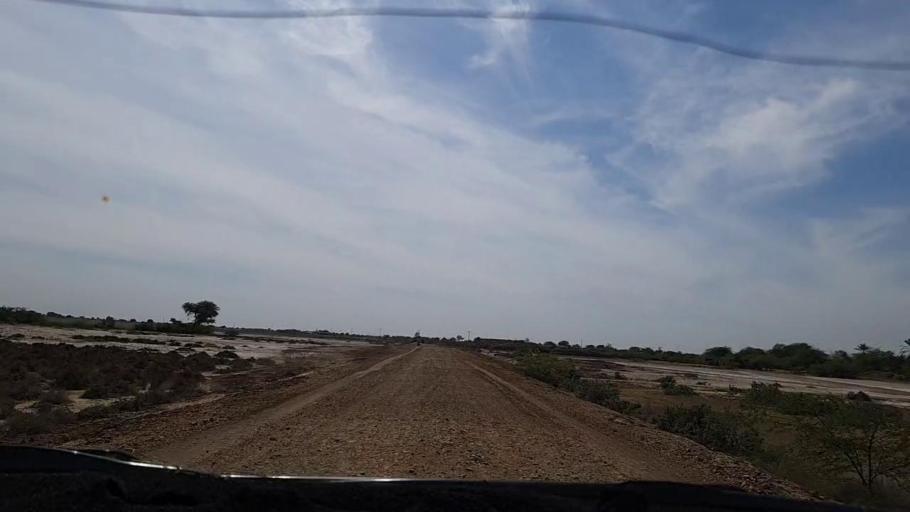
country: PK
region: Sindh
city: Pithoro
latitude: 25.4980
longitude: 69.4583
